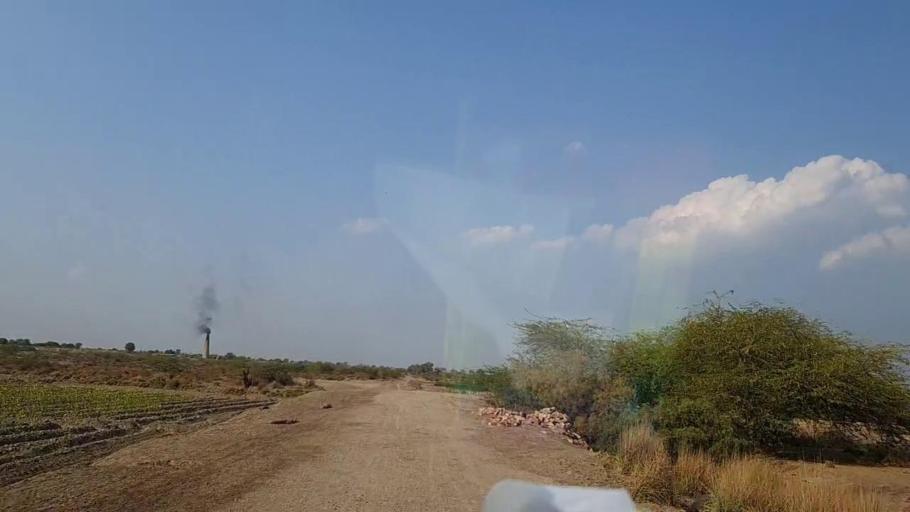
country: PK
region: Sindh
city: Nawabshah
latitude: 26.1628
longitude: 68.4134
